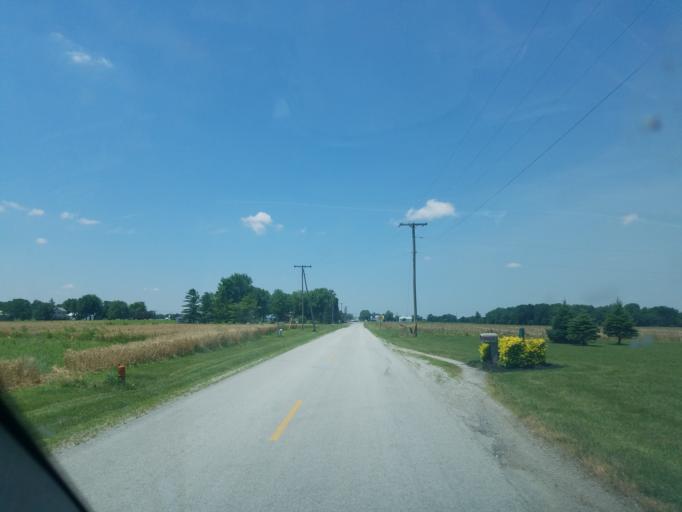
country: US
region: Ohio
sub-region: Hardin County
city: Kenton
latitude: 40.7315
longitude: -83.6235
